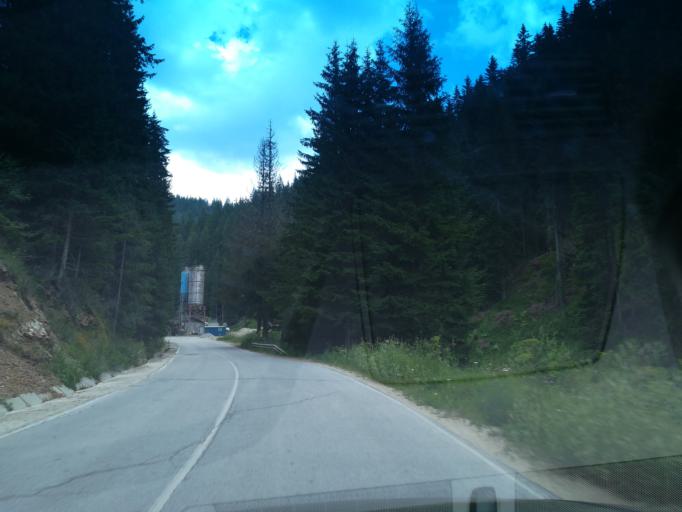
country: BG
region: Smolyan
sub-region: Obshtina Chepelare
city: Chepelare
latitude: 41.6608
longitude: 24.6752
